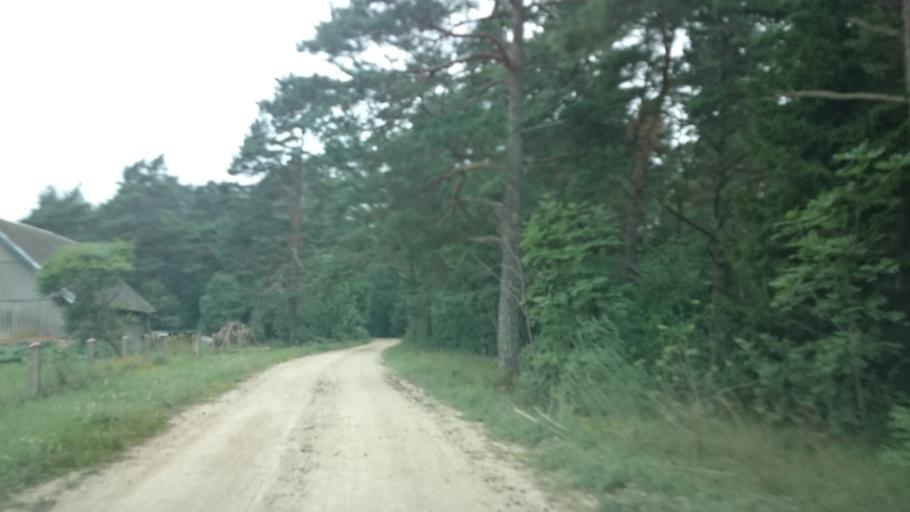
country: EE
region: Saare
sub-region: Orissaare vald
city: Orissaare
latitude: 58.5947
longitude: 22.7038
